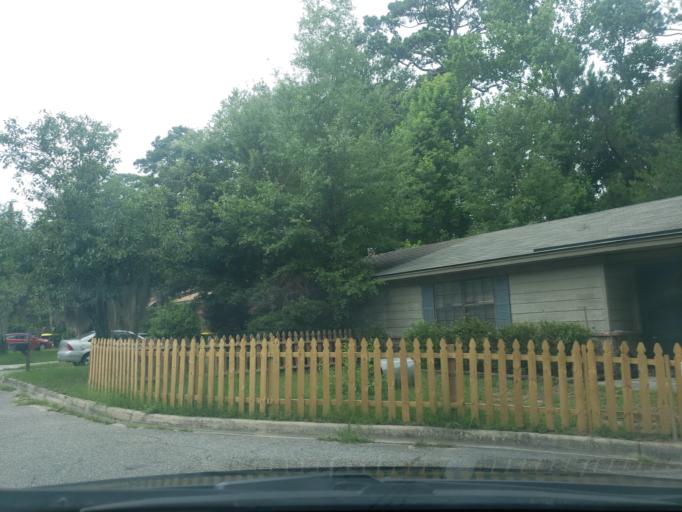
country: US
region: Georgia
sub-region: Chatham County
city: Montgomery
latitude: 31.9885
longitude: -81.1166
